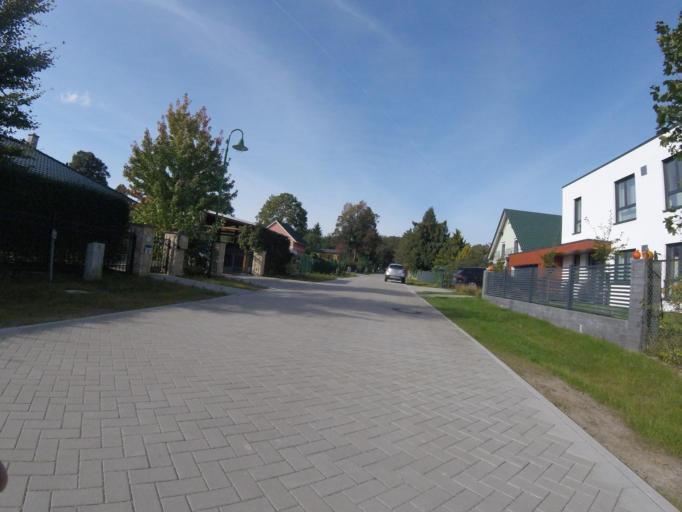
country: DE
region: Brandenburg
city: Konigs Wusterhausen
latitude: 52.2960
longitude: 13.6921
